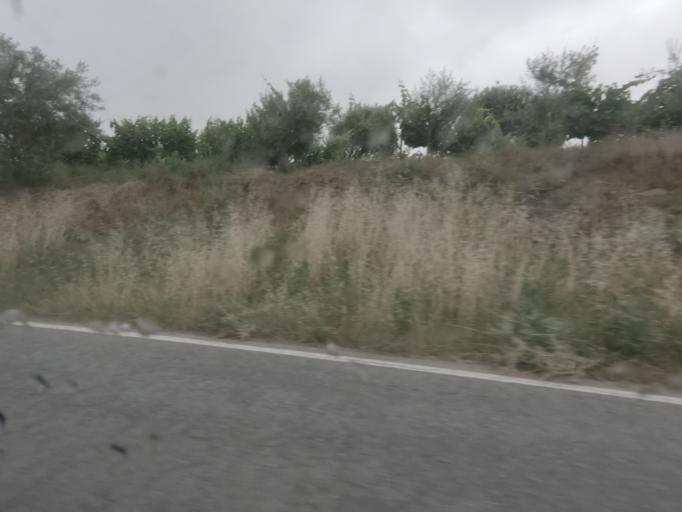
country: PT
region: Vila Real
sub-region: Peso da Regua
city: Peso da Regua
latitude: 41.1300
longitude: -7.7494
